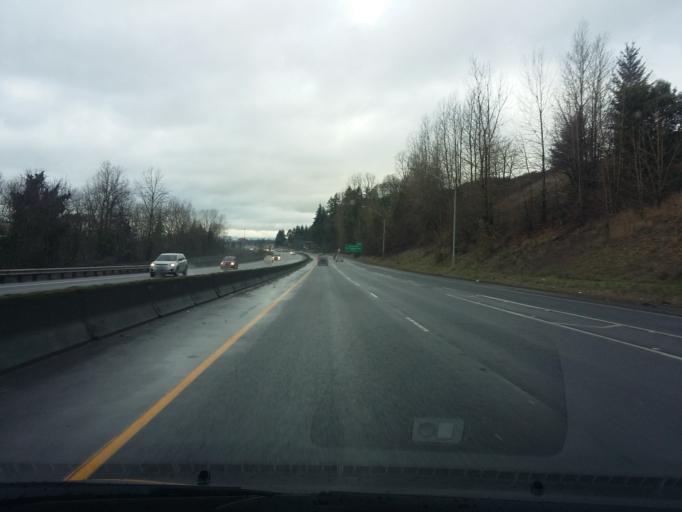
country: US
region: Washington
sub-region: Clark County
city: Vancouver
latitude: 45.6167
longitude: -122.6174
